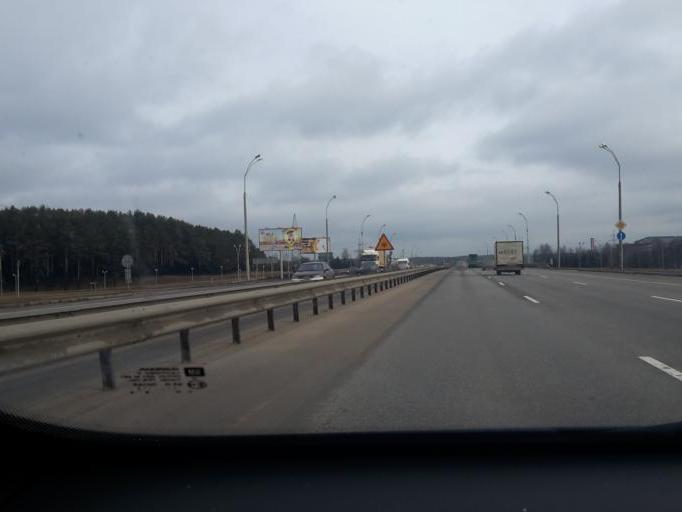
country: BY
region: Minsk
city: Zhdanovichy
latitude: 53.9492
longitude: 27.4435
